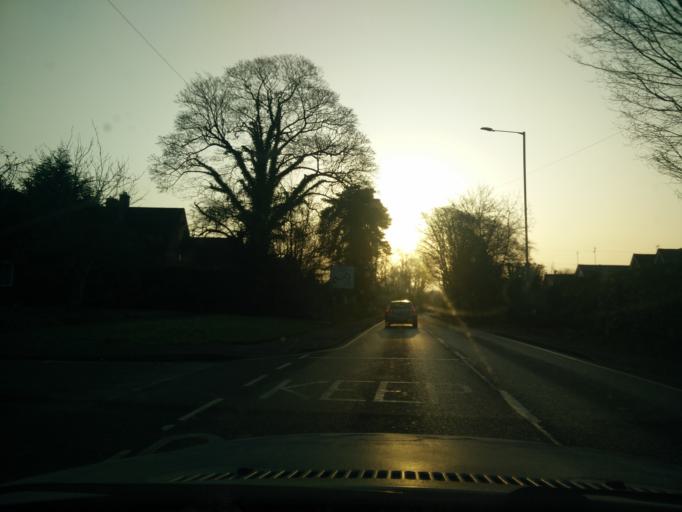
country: GB
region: England
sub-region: Buckinghamshire
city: Amersham on the Hill
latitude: 51.6739
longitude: -0.5940
